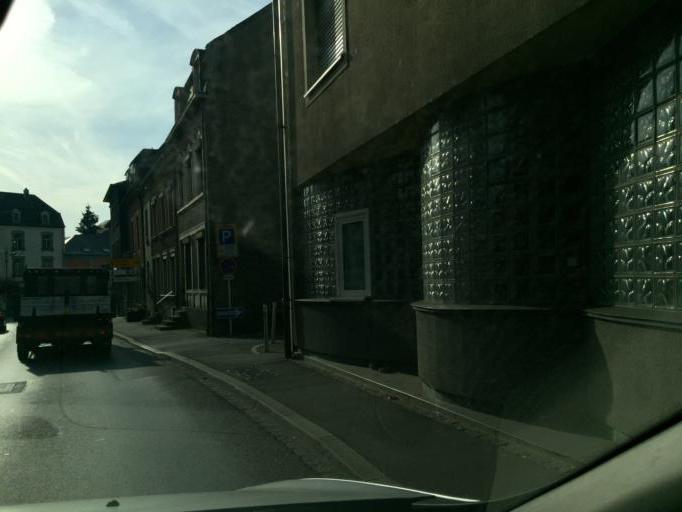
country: LU
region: Diekirch
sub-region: Canton de Diekirch
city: Diekirch
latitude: 49.8678
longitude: 6.1590
